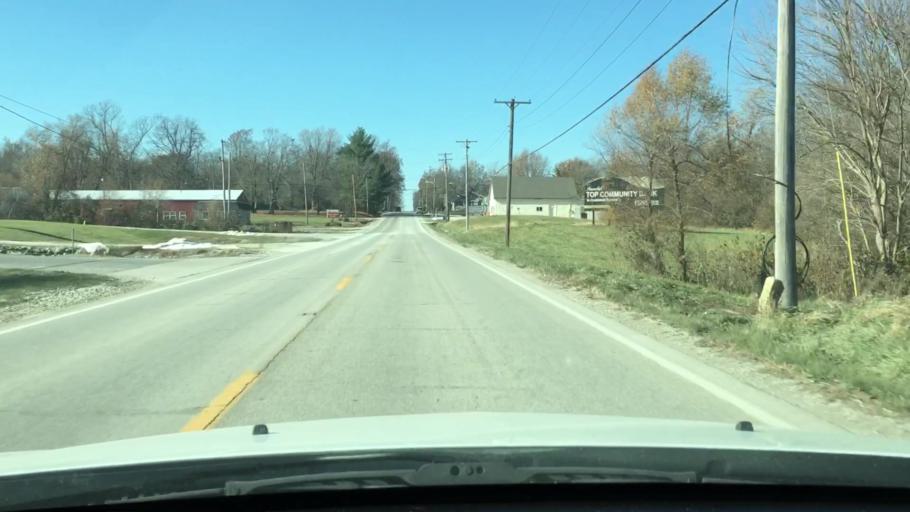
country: US
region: Illinois
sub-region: Pike County
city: Pittsfield
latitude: 39.6068
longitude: -90.7885
